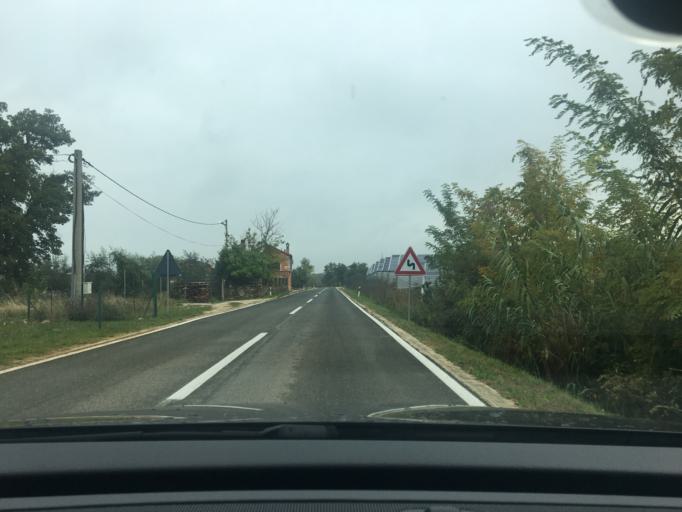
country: HR
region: Istarska
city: Buje
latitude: 45.4206
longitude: 13.6620
